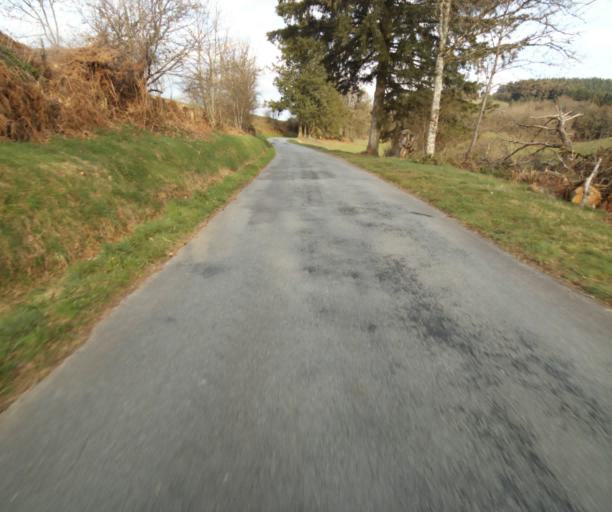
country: FR
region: Limousin
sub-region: Departement de la Correze
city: Correze
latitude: 45.4139
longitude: 1.9111
